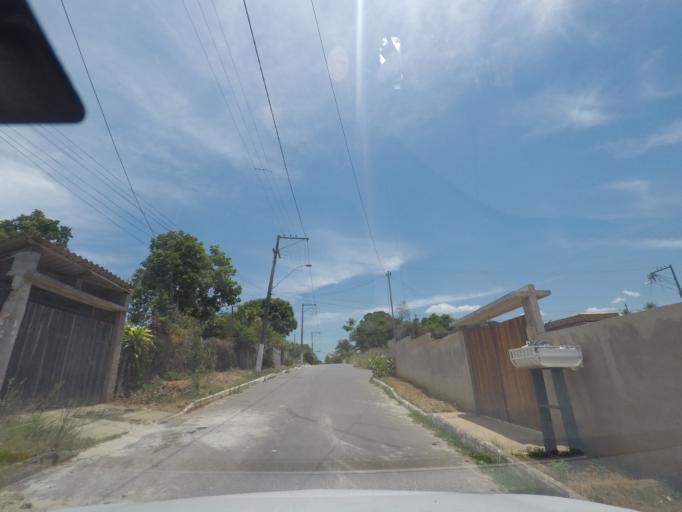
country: BR
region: Rio de Janeiro
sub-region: Marica
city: Marica
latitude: -22.9299
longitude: -42.8247
